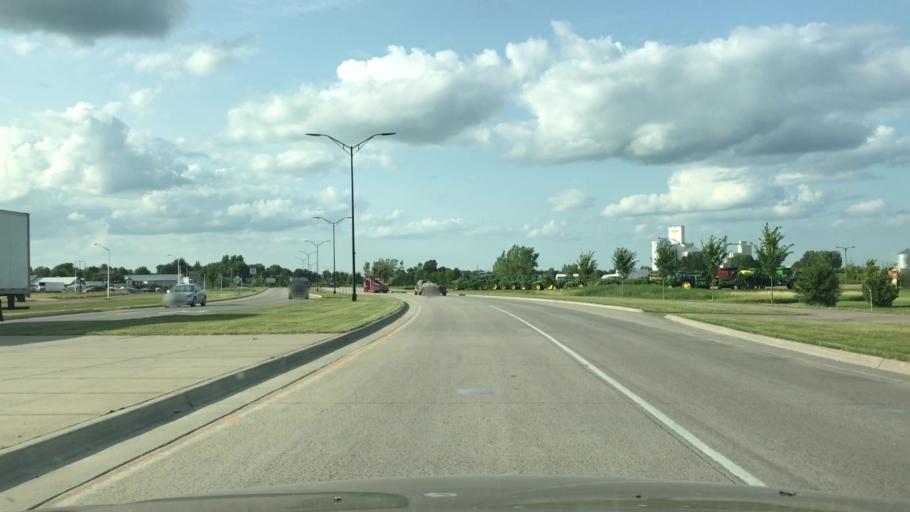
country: US
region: Minnesota
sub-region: Nobles County
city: Worthington
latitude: 43.6213
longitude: -95.5795
